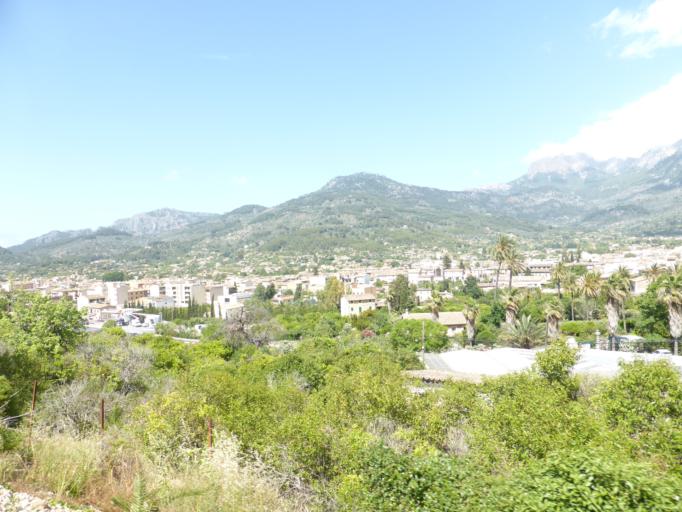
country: ES
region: Balearic Islands
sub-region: Illes Balears
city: Soller
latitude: 39.7631
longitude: 2.7088
